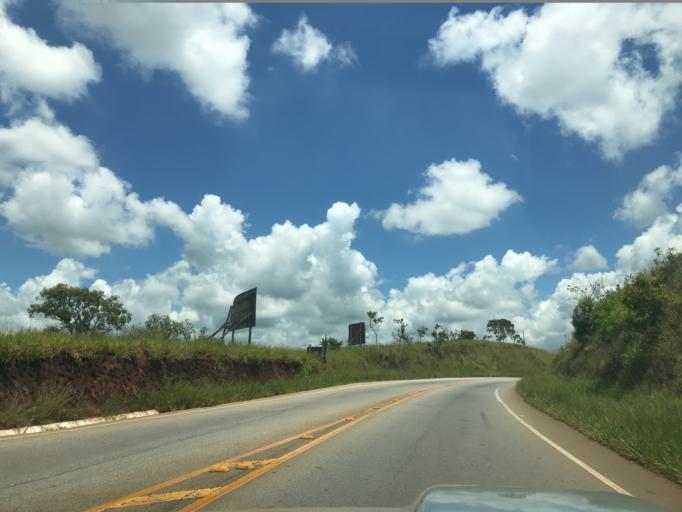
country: BR
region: Minas Gerais
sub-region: Tres Coracoes
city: Tres Coracoes
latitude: -21.6586
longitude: -45.2981
